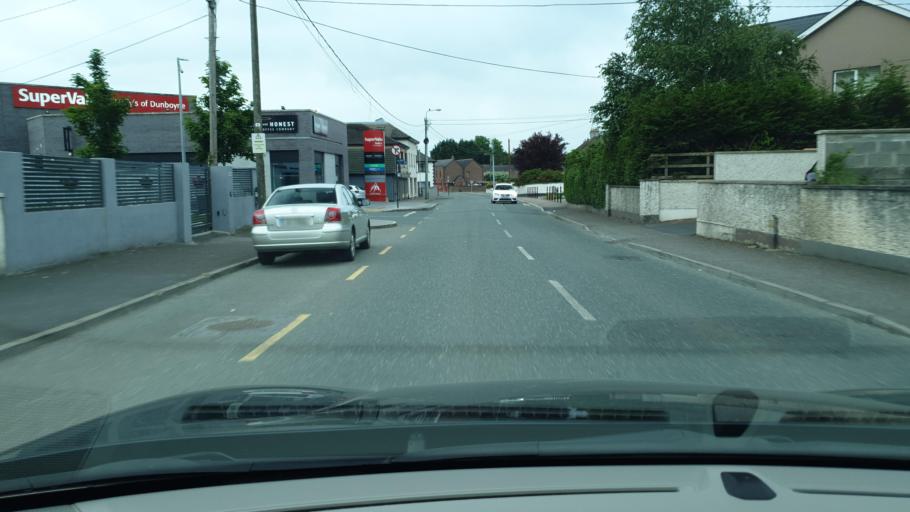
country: IE
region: Leinster
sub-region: An Mhi
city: Dunboyne
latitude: 53.4222
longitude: -6.4747
